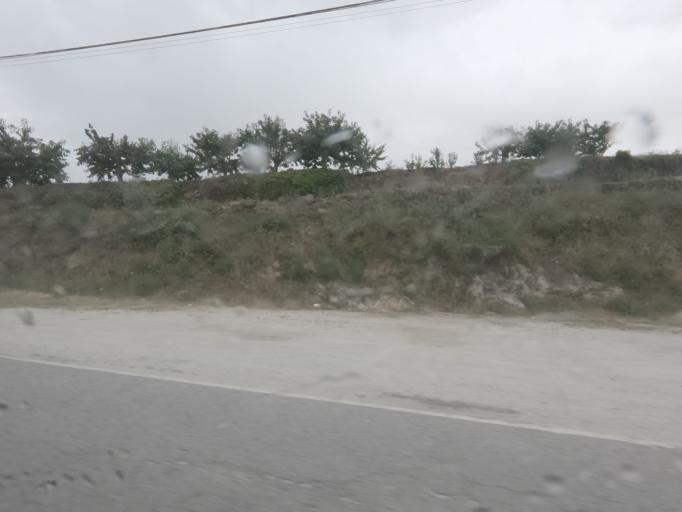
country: PT
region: Viseu
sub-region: Armamar
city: Armamar
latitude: 41.1158
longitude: -7.7257
